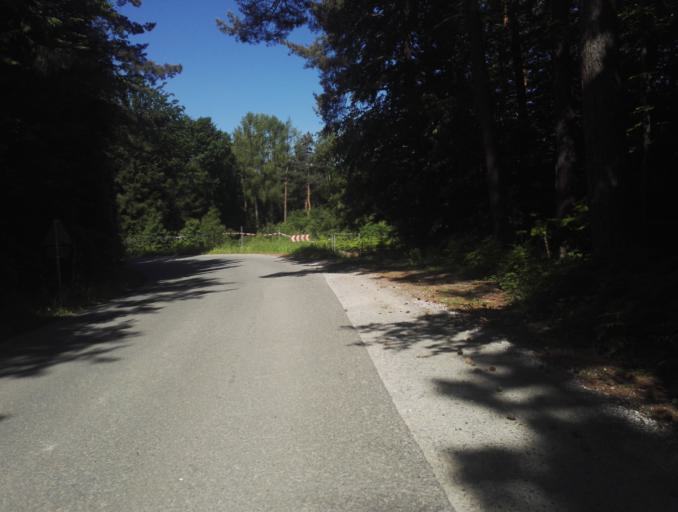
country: AT
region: Styria
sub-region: Politischer Bezirk Graz-Umgebung
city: Edelsgrub
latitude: 47.0504
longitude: 15.5623
